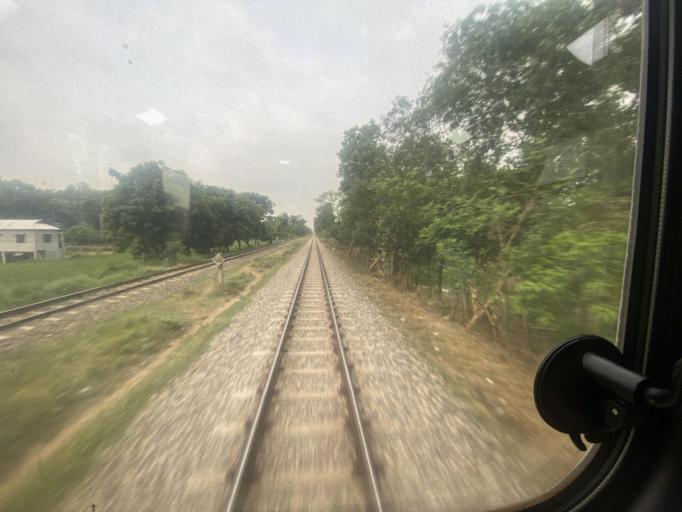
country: BD
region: Dhaka
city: Tungi
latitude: 23.9231
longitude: 90.4435
